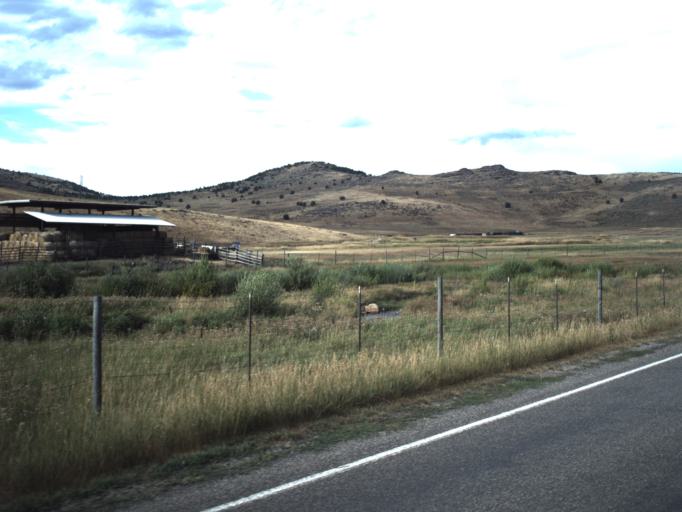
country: US
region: Utah
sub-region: Cache County
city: Millville
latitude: 41.6024
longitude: -111.5644
